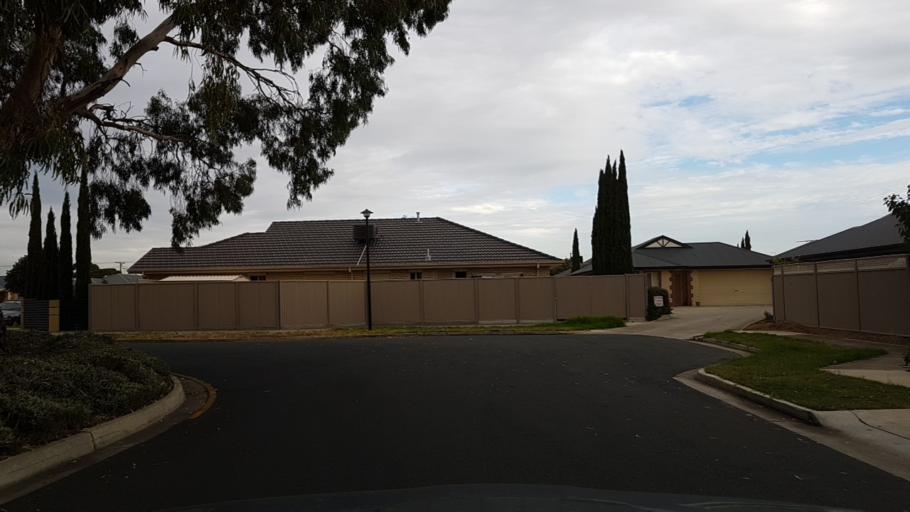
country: AU
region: South Australia
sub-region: Charles Sturt
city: Woodville North
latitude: -34.8608
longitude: 138.5412
